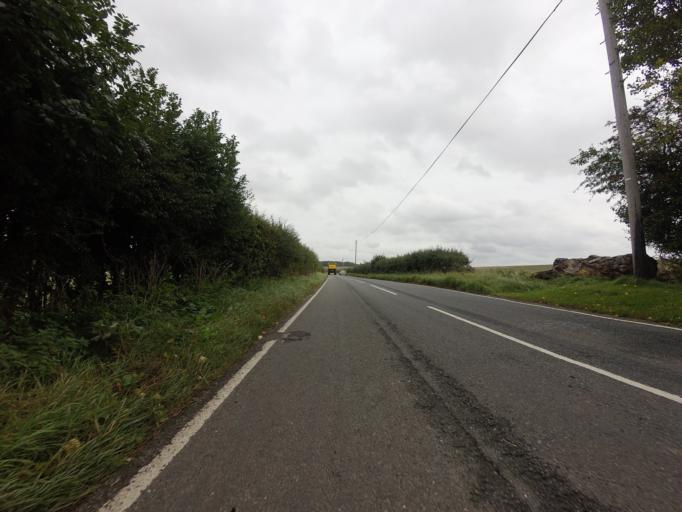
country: GB
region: England
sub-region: Cambridgeshire
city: Duxford
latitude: 52.0202
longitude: 0.1363
